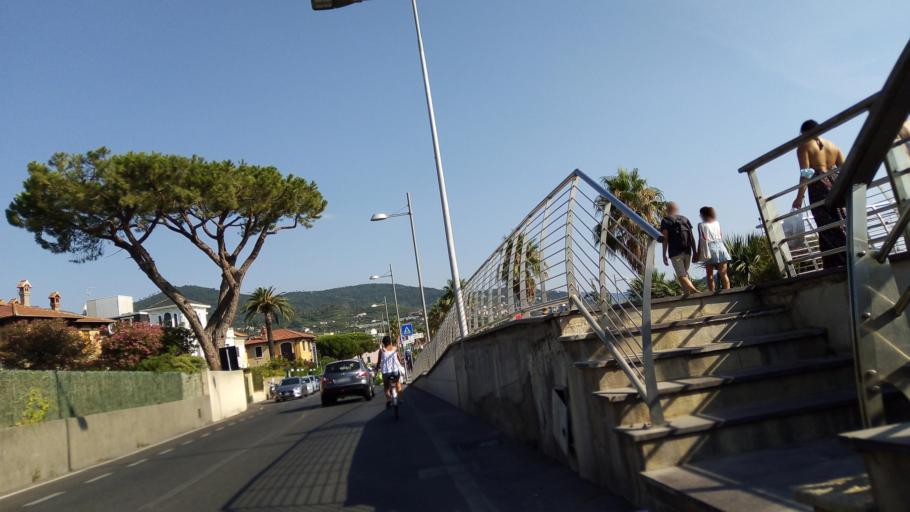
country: IT
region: Liguria
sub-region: Provincia di Savona
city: Loano
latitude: 44.1305
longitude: 8.2630
